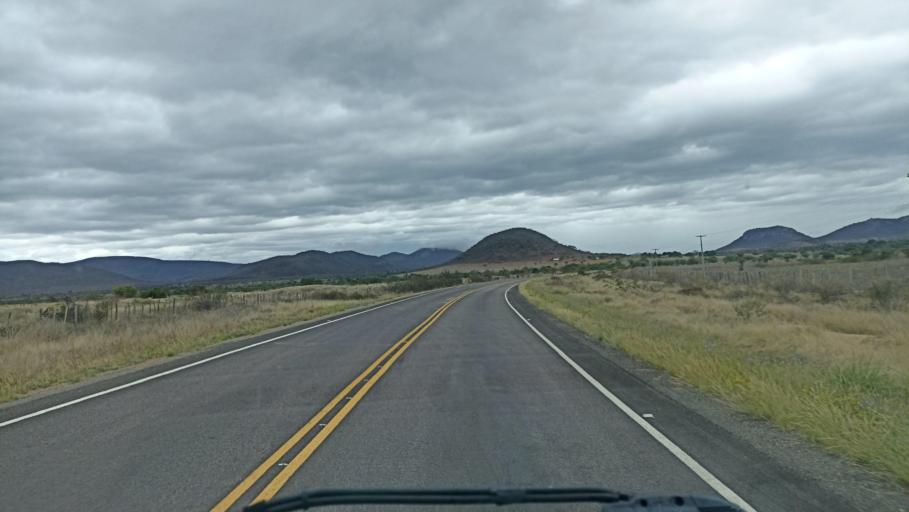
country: BR
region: Bahia
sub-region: Iacu
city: Iacu
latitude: -12.9228
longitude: -40.4162
